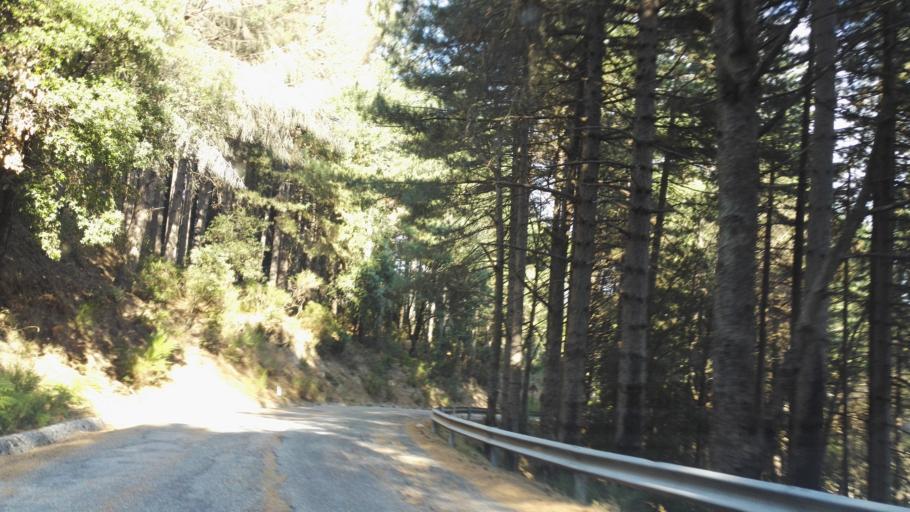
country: IT
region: Calabria
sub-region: Provincia di Vibo-Valentia
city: Nardodipace
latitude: 38.4626
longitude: 16.3520
